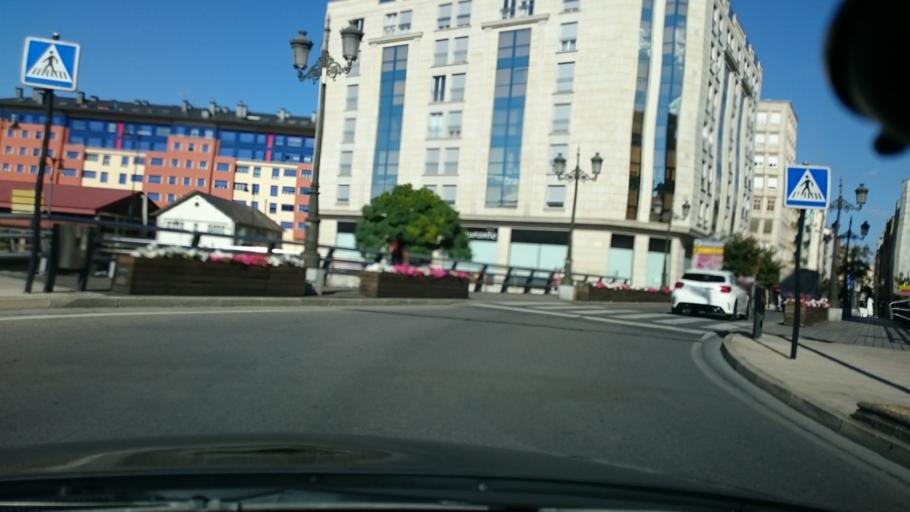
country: ES
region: Castille and Leon
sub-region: Provincia de Leon
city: Ponferrada
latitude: 42.5468
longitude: -6.6046
